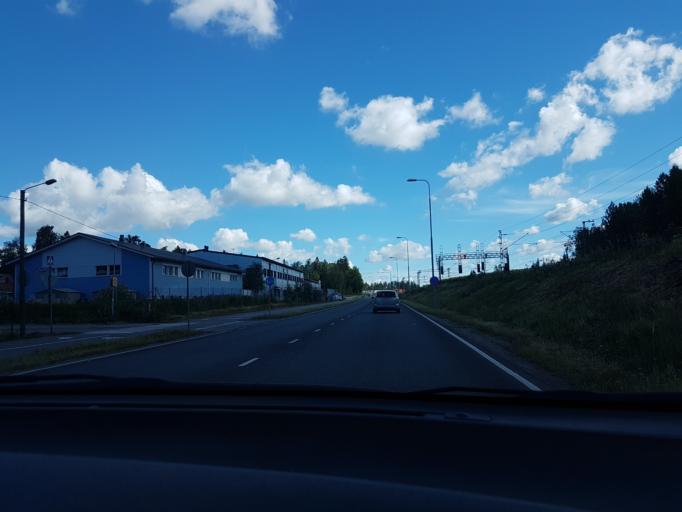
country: FI
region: Uusimaa
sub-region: Helsinki
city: Kerava
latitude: 60.3698
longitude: 25.0921
